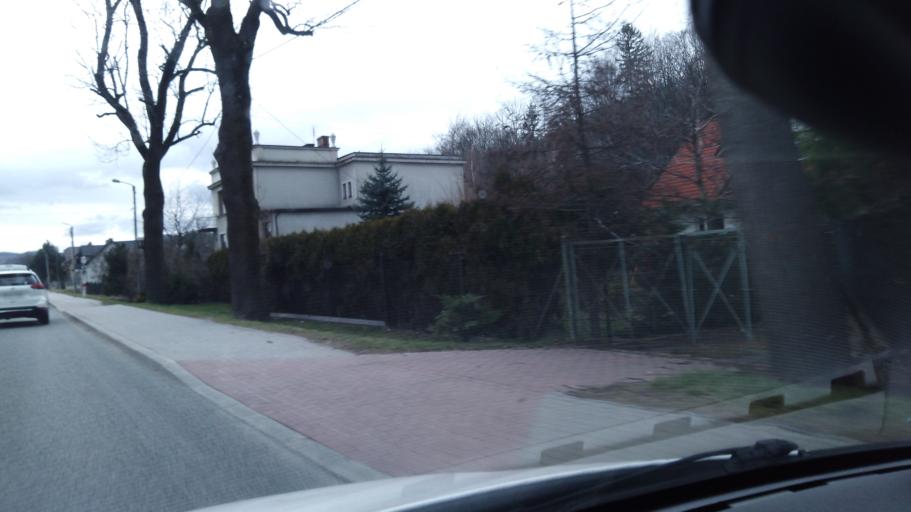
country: PL
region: Silesian Voivodeship
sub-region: Powiat zywiecki
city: Wegierska Gorka
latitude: 49.6152
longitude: 19.1227
